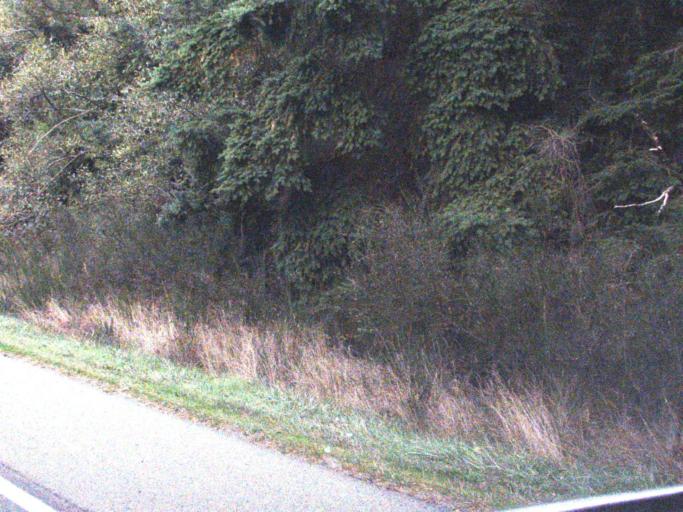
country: US
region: Washington
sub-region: Island County
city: Langley
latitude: 48.0036
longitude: -122.4331
